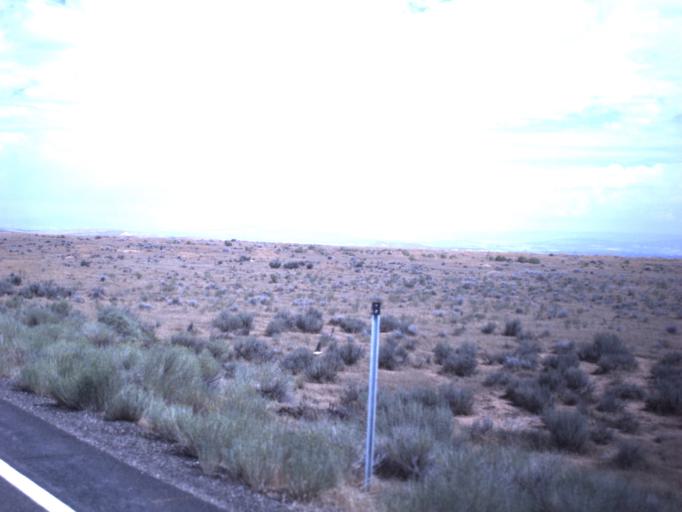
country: US
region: Utah
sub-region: Uintah County
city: Naples
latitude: 40.2475
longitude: -109.4218
